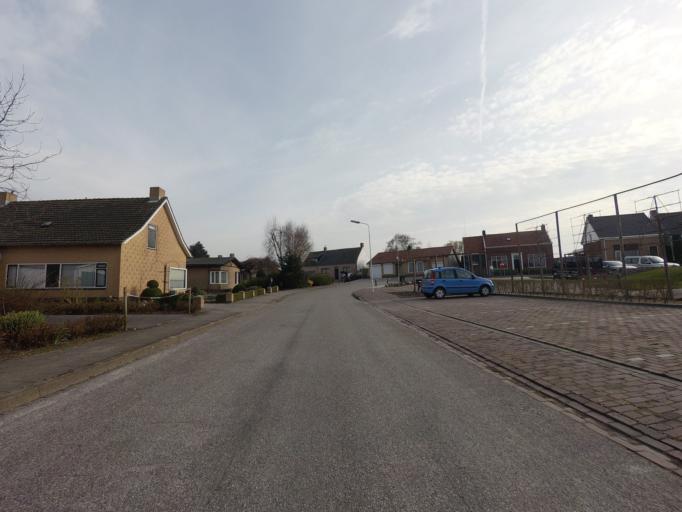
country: NL
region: Zeeland
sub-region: Gemeente Terneuzen
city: Zaamslag
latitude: 51.3878
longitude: 3.9811
